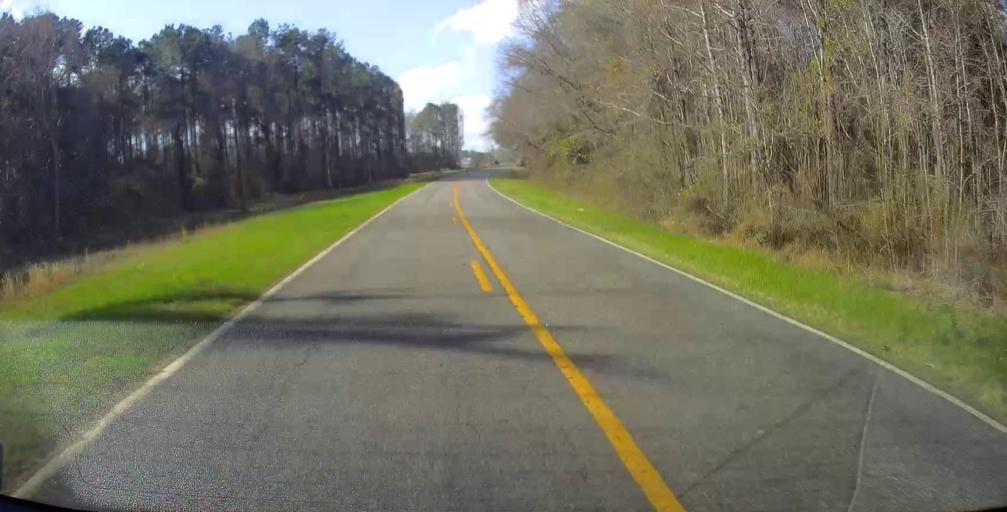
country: US
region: Georgia
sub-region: Laurens County
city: Dublin
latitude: 32.5952
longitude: -83.0693
